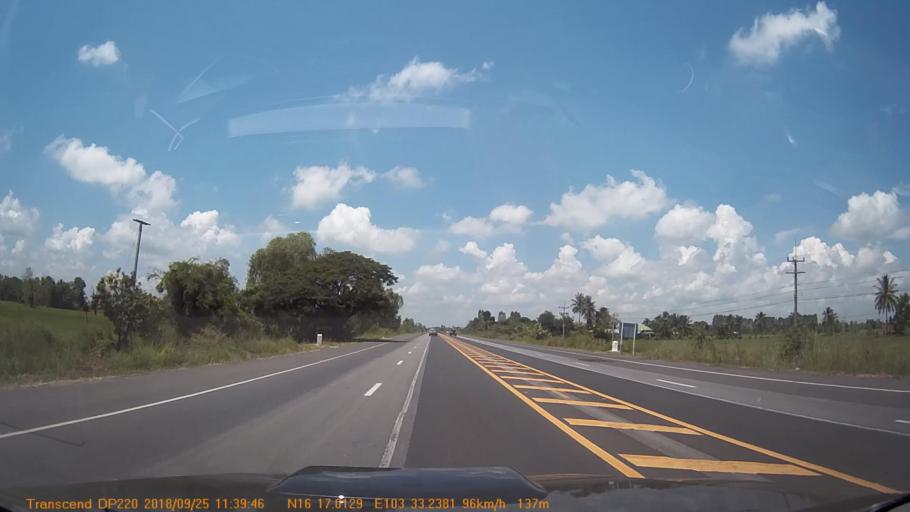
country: TH
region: Kalasin
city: Kamalasai
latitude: 16.2834
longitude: 103.5539
